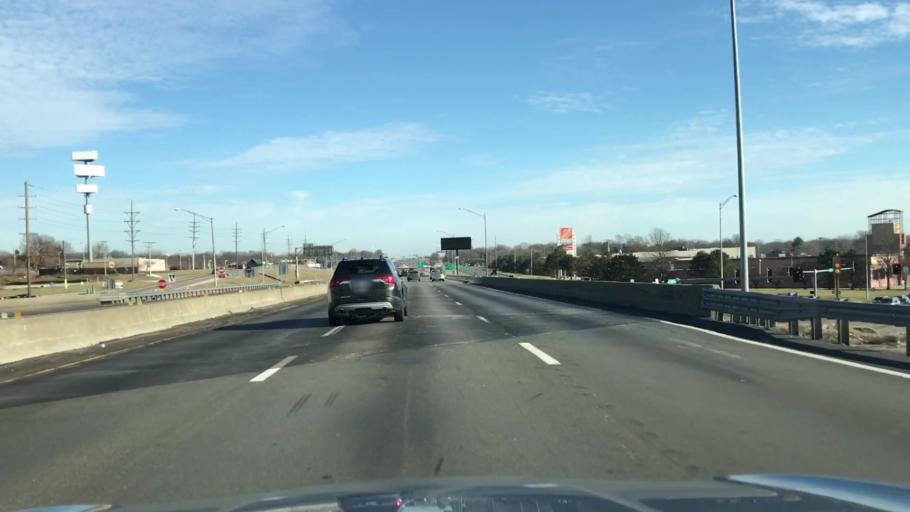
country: US
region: Missouri
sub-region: Saint Louis County
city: Black Jack
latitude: 38.7710
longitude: -90.2674
